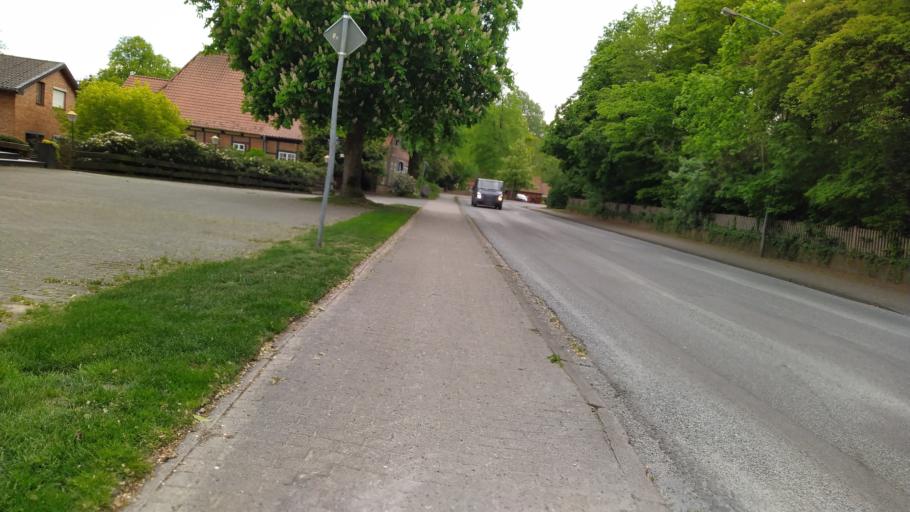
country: DE
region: Lower Saxony
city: Kirchtimke
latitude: 53.2519
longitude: 9.1522
